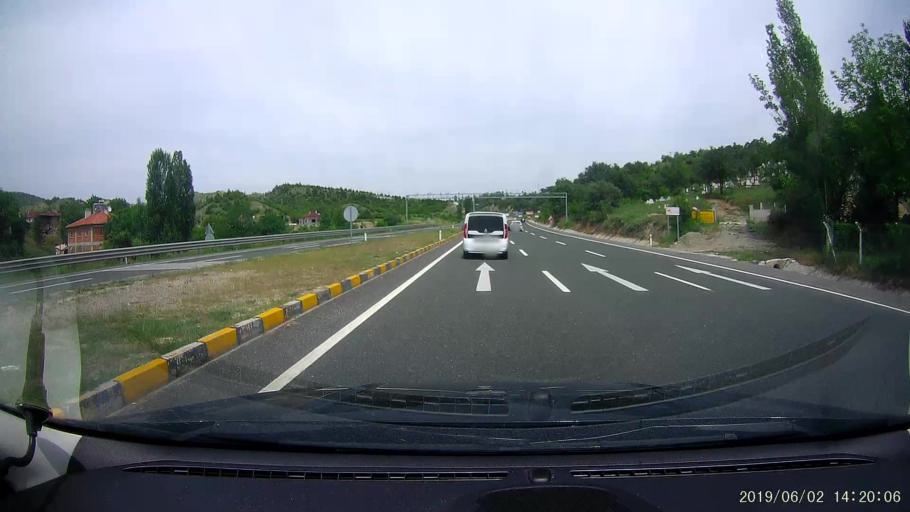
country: TR
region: Kastamonu
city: Tosya
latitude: 40.9682
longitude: 33.9850
